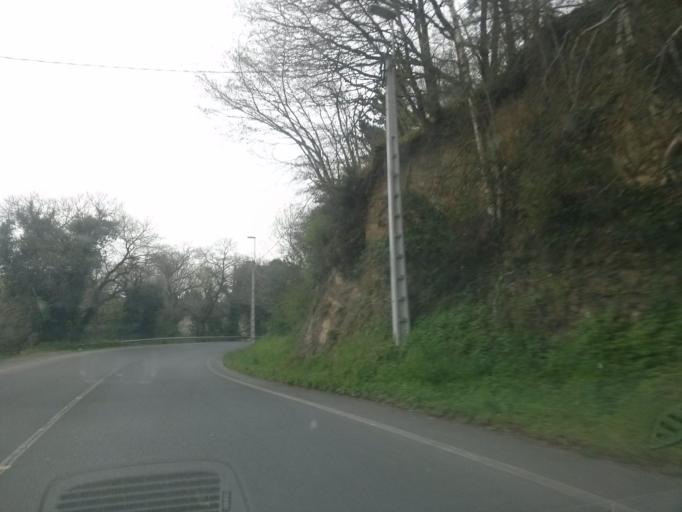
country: ES
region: Galicia
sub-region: Provincia de Lugo
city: Lugo
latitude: 43.0263
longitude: -7.5447
